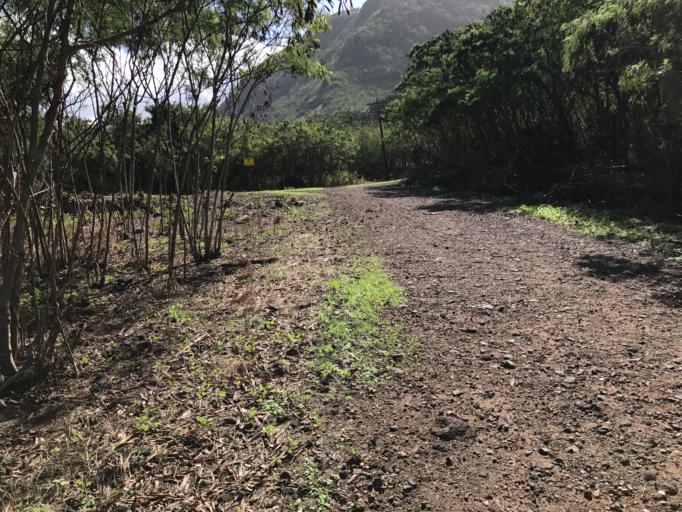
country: US
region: Hawaii
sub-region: Honolulu County
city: Mokuleia
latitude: 21.5755
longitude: -158.2069
